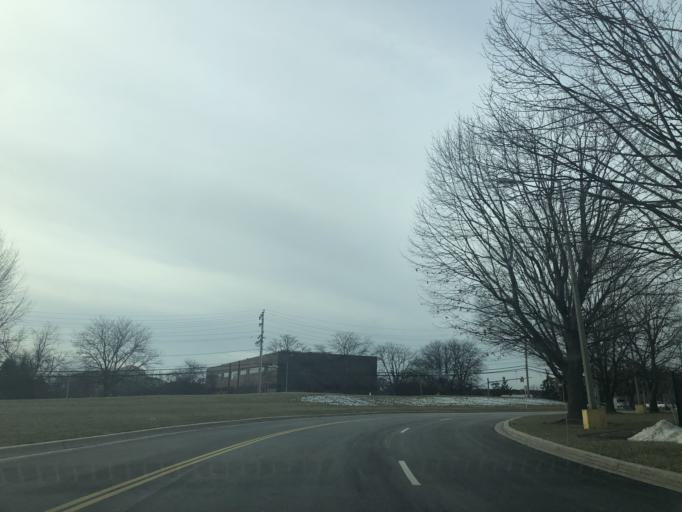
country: US
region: Maryland
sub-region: Anne Arundel County
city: Linthicum
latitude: 39.2046
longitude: -76.6831
